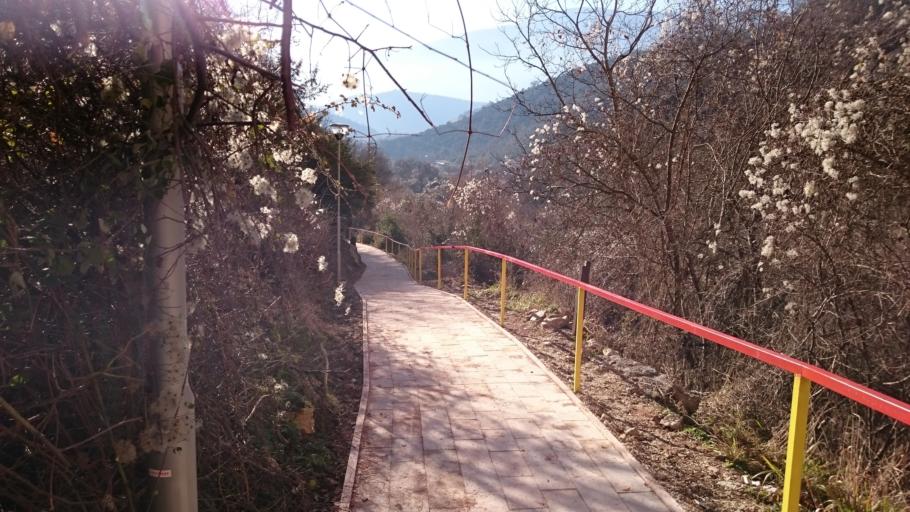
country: MK
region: Makedonski Brod
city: Makedonski Brod
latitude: 41.5478
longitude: 21.2521
